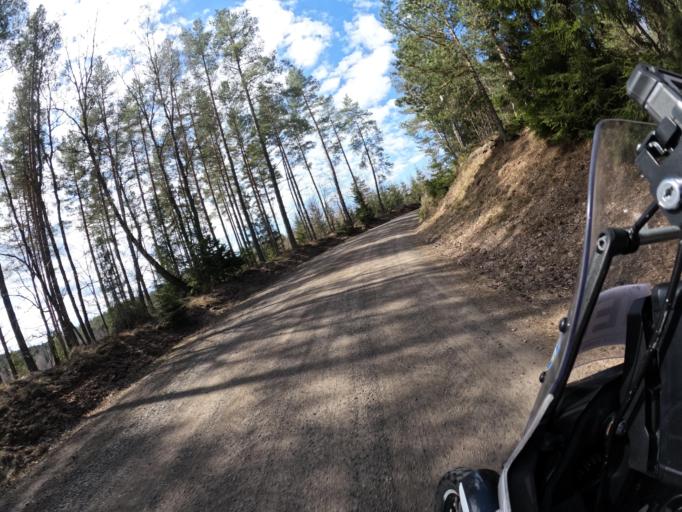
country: SE
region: Joenkoeping
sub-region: Mullsjo Kommun
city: Mullsjoe
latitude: 57.9926
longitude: 13.8370
